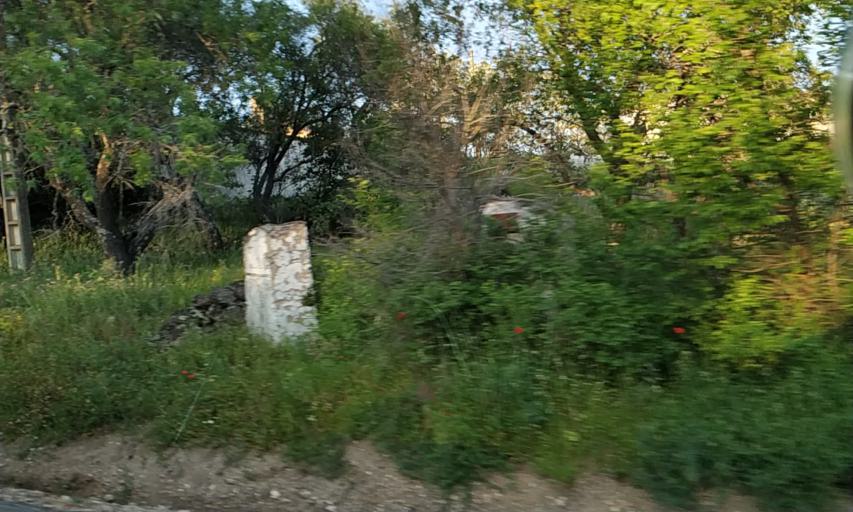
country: ES
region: Extremadura
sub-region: Provincia de Caceres
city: Valencia de Alcantara
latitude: 39.4010
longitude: -7.2509
